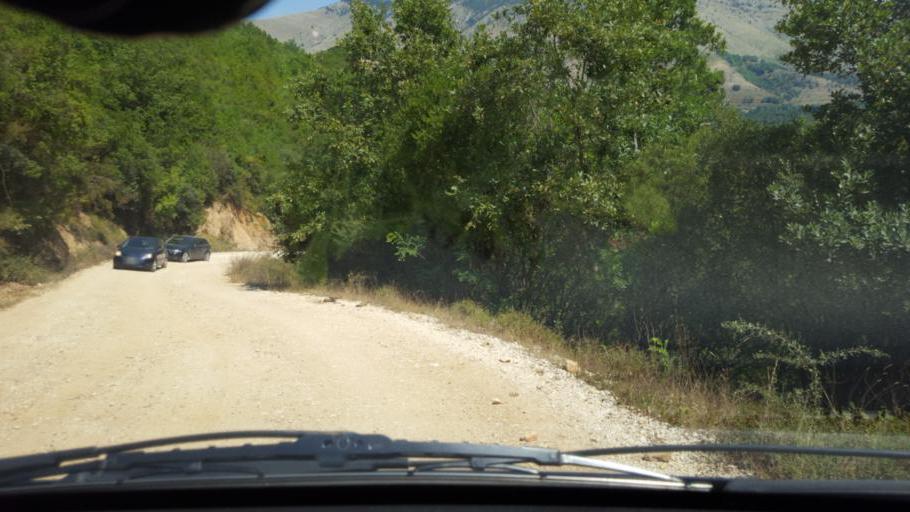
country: AL
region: Vlore
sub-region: Rrethi i Sarandes
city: Dhiver
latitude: 39.9206
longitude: 20.1870
